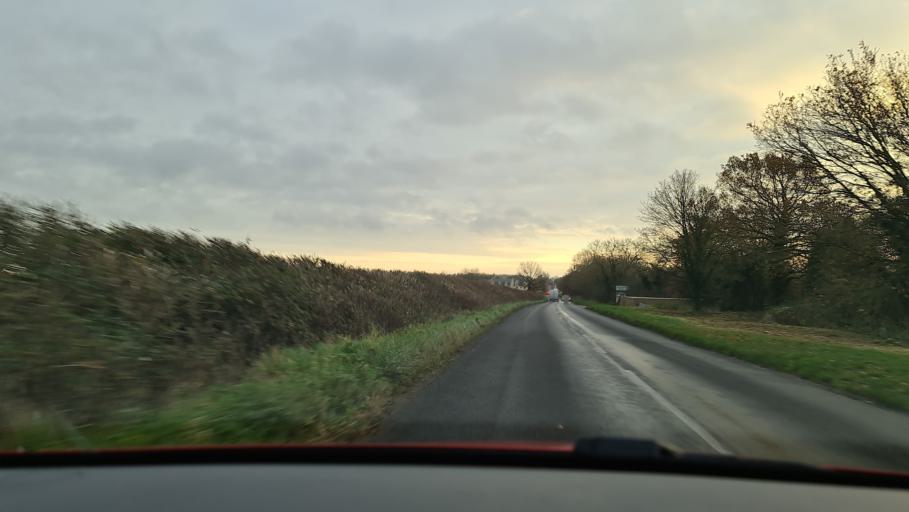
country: GB
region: England
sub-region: Oxfordshire
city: Kidlington
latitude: 51.8570
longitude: -1.2844
